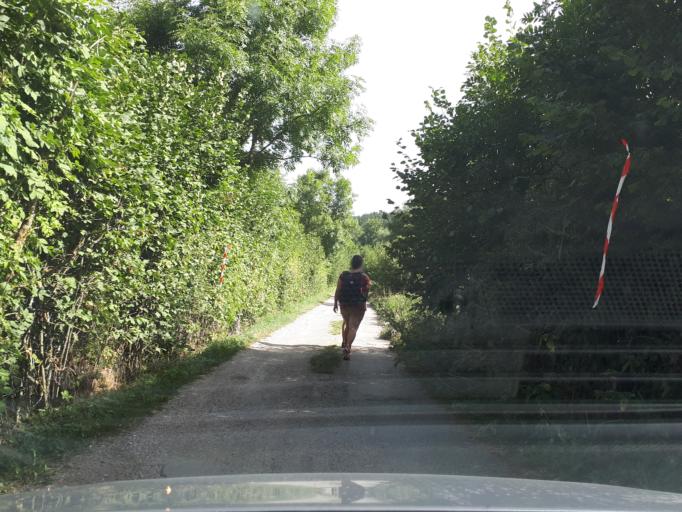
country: FR
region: Rhone-Alpes
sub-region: Departement de l'Isere
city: Pierre-Chatel
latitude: 44.9856
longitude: 5.7828
